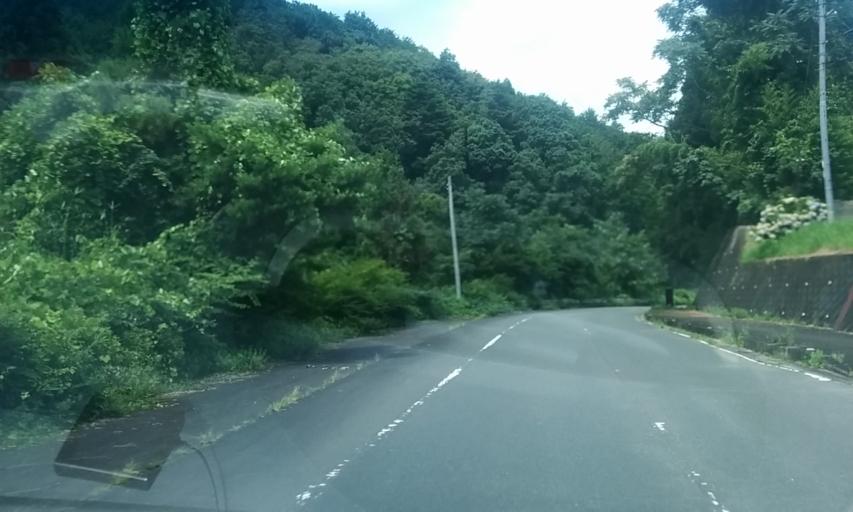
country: JP
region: Kyoto
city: Ayabe
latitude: 35.1968
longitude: 135.2465
